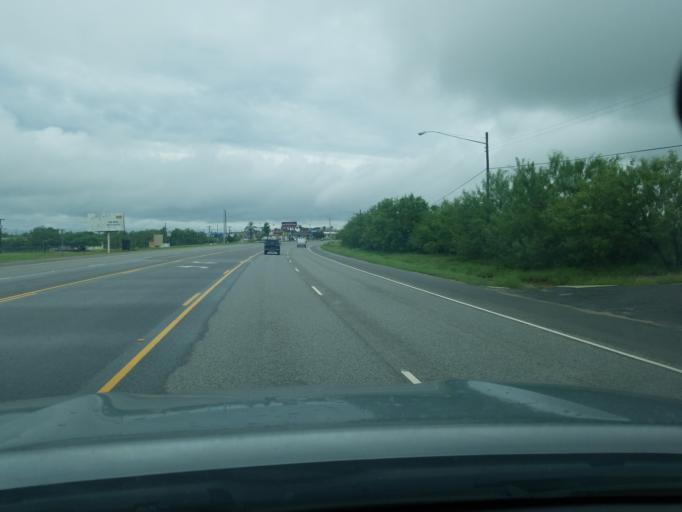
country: US
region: Texas
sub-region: Dimmit County
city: Carrizo Springs
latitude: 28.5381
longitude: -99.8500
